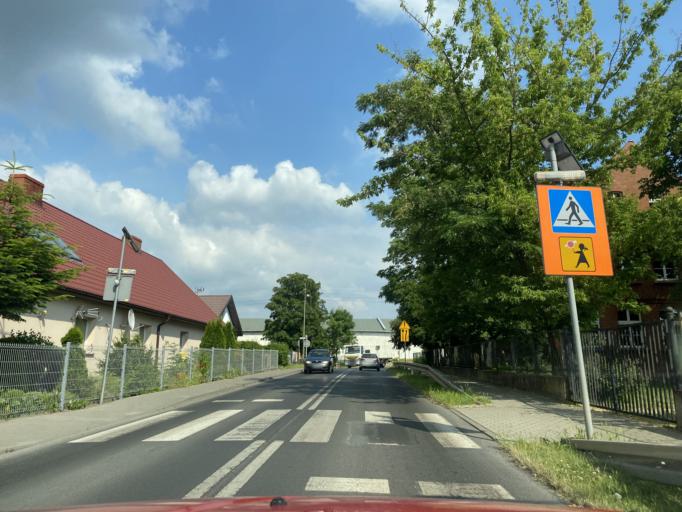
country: PL
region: Greater Poland Voivodeship
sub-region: Powiat poznanski
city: Dopiewo
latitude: 52.3599
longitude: 16.7095
